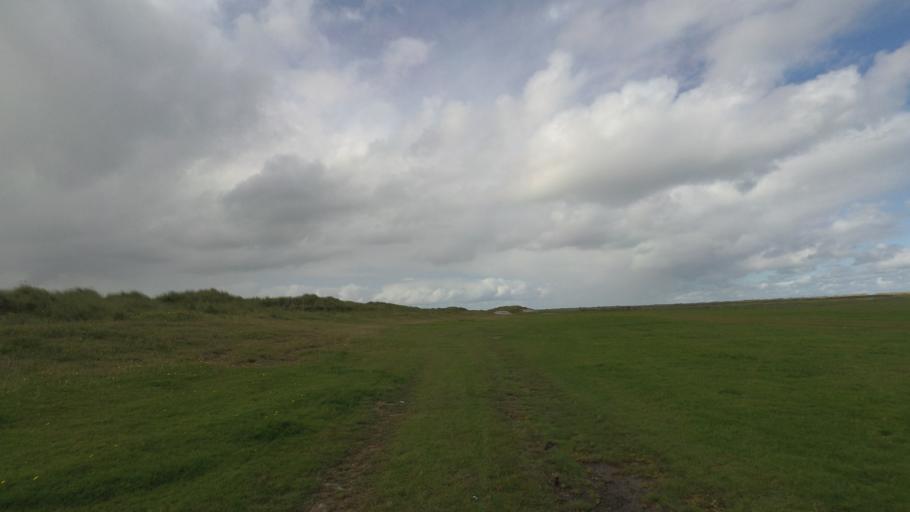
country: NL
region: Friesland
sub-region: Gemeente Ameland
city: Nes
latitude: 53.4495
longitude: 5.8616
